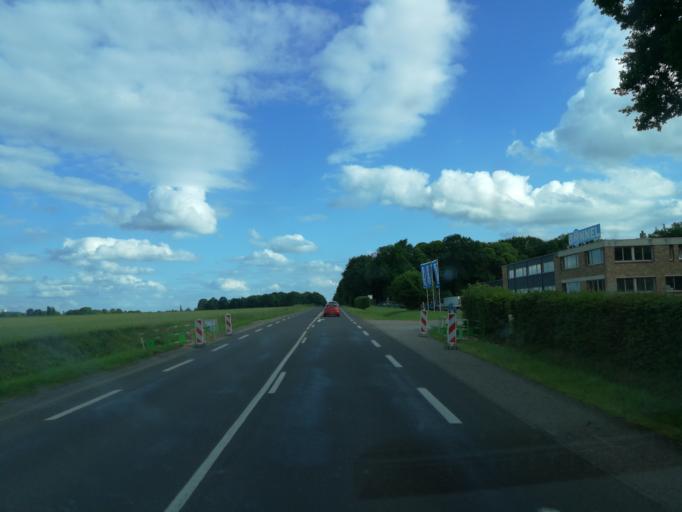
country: FR
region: Haute-Normandie
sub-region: Departement de l'Eure
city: Le Neubourg
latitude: 49.1323
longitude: 0.9065
